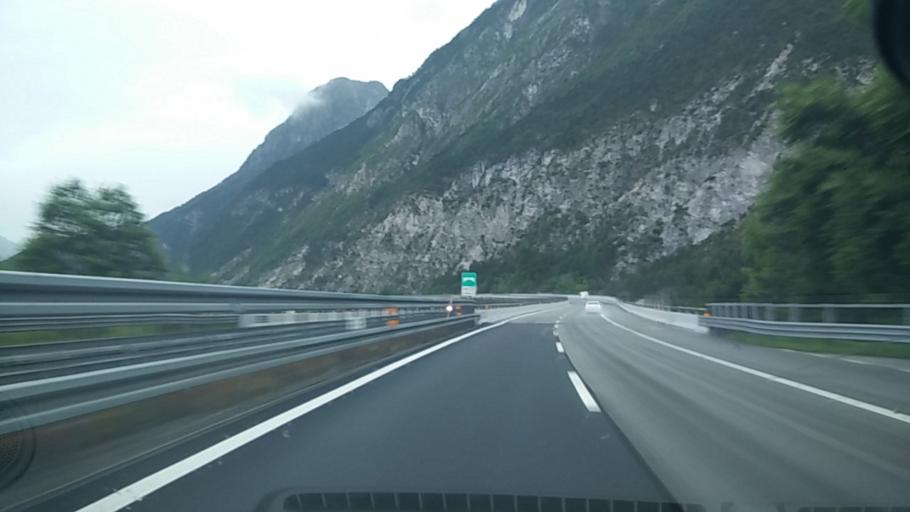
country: IT
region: Friuli Venezia Giulia
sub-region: Provincia di Udine
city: Pontebba
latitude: 46.5082
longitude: 13.3537
